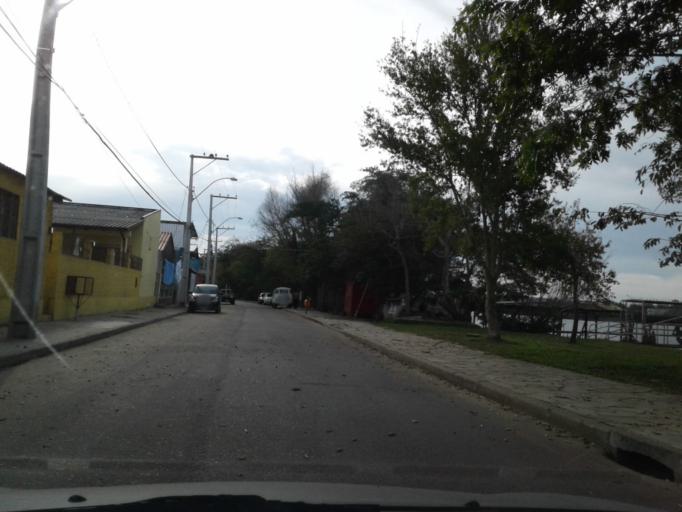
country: BR
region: Rio Grande do Sul
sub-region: Porto Alegre
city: Porto Alegre
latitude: -30.0169
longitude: -51.2575
